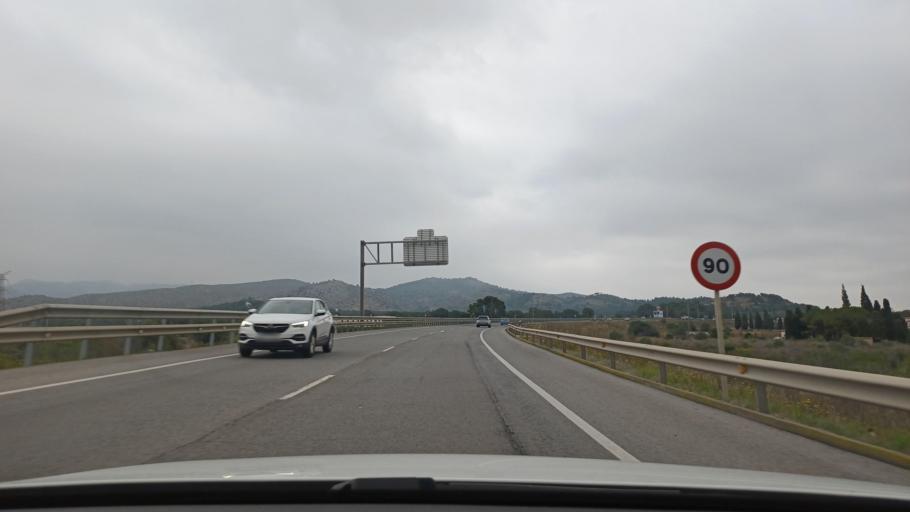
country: ES
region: Valencia
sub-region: Provincia de Castello
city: Borriol
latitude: 39.9991
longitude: -0.0863
